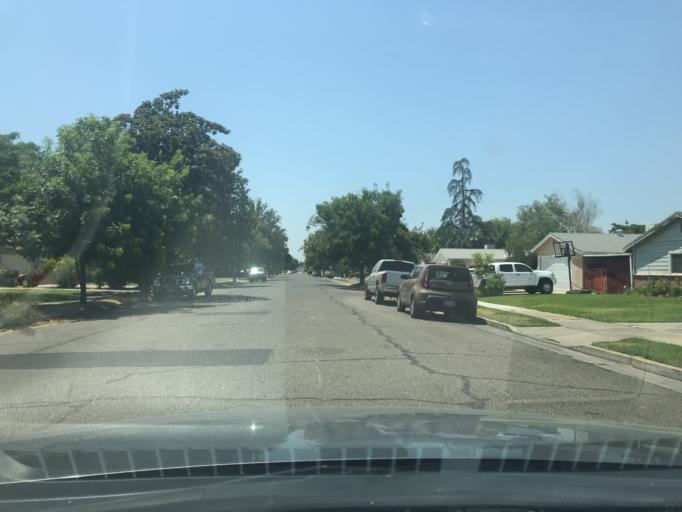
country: US
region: California
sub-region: Merced County
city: Atwater
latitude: 37.3589
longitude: -120.6057
